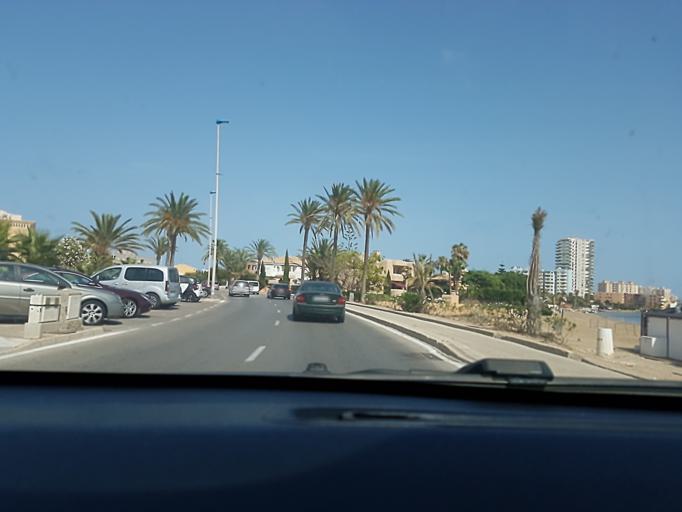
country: ES
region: Murcia
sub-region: Murcia
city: La Manga del Mar Menor
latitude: 37.6612
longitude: -0.7276
